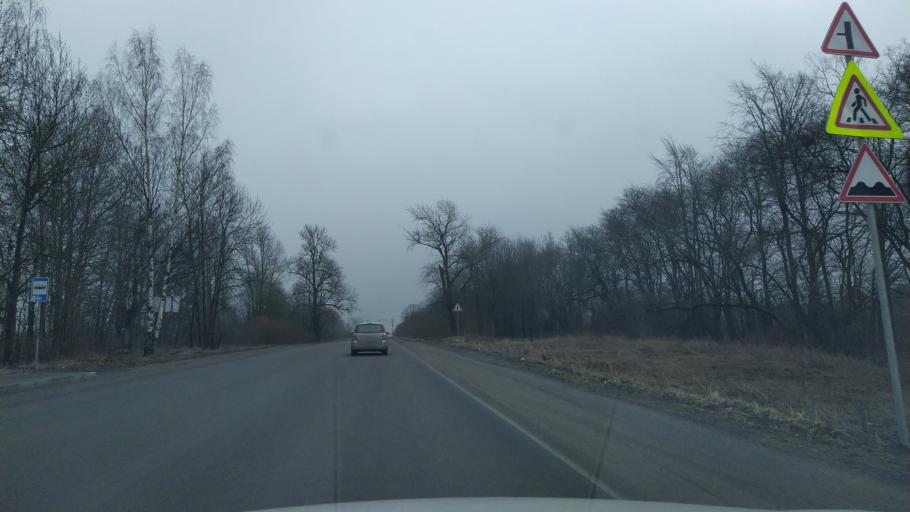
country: RU
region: St.-Petersburg
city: Gorelovo
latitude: 59.7295
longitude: 30.1512
